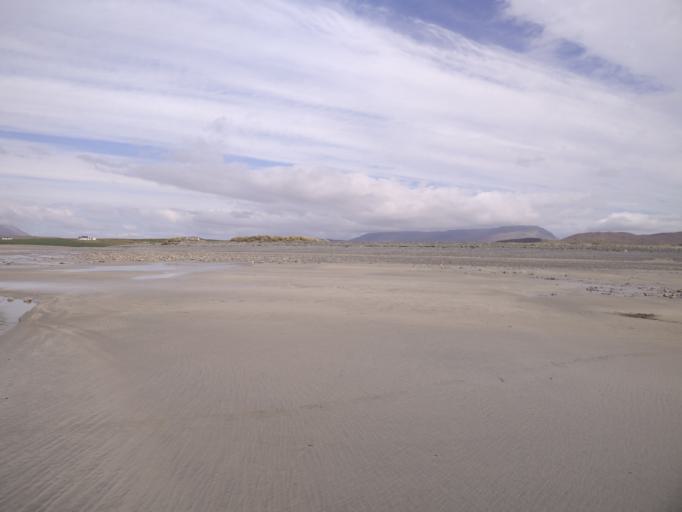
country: IE
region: Connaught
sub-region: County Galway
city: Clifden
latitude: 53.7242
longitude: -9.9001
